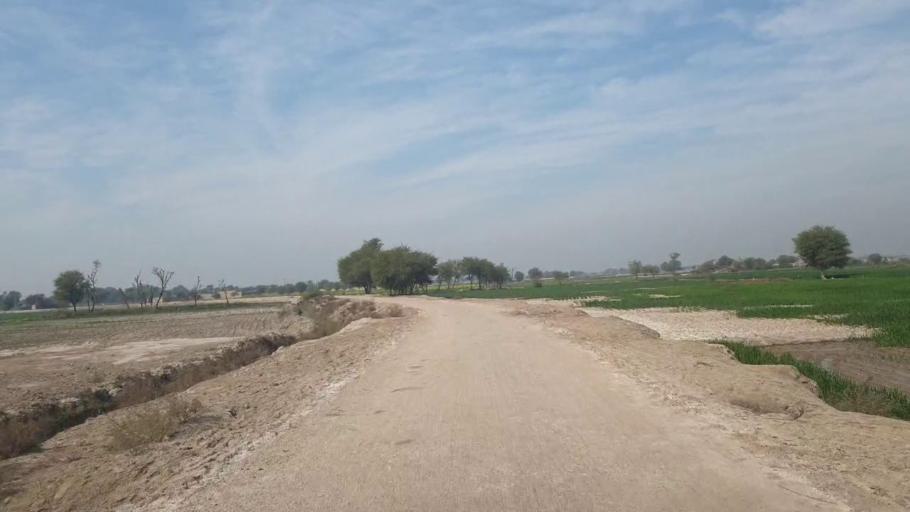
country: PK
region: Sindh
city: Nawabshah
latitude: 26.1631
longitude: 68.5054
